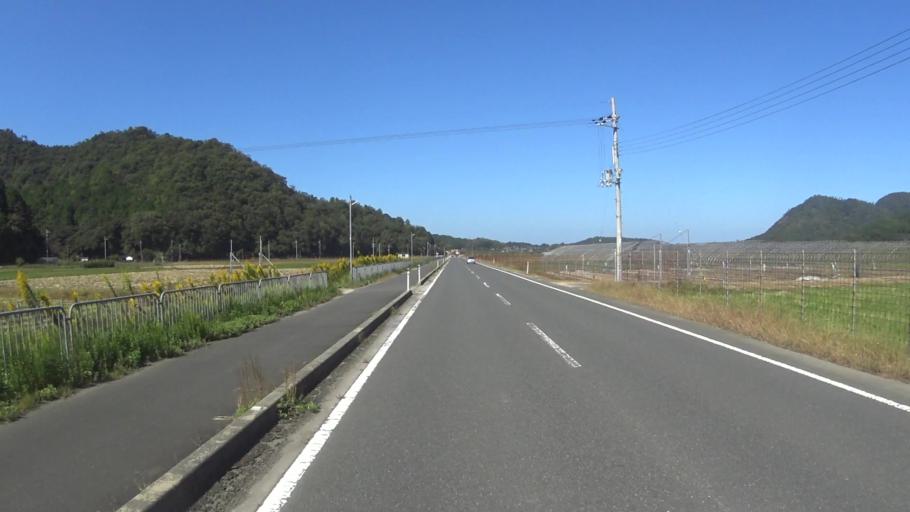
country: JP
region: Hyogo
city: Toyooka
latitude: 35.6020
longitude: 134.9235
